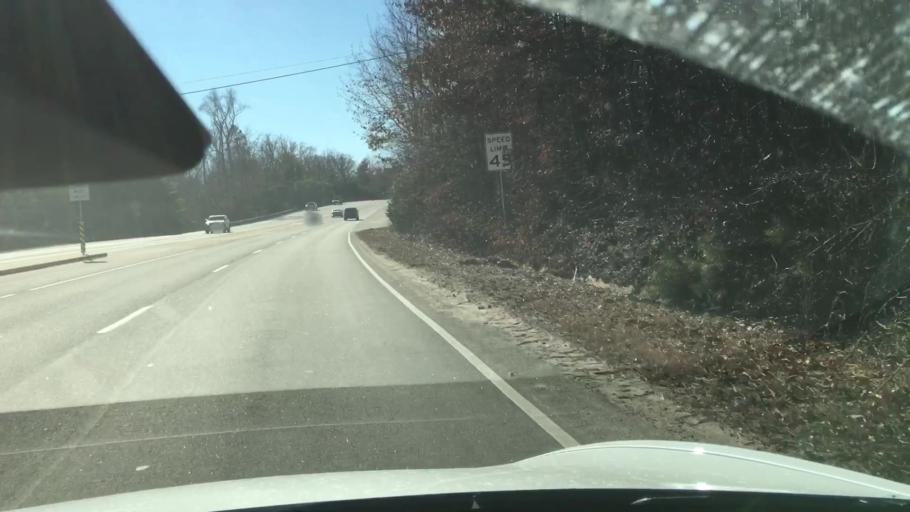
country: US
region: Virginia
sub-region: Chesterfield County
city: Bon Air
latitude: 37.5426
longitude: -77.5550
